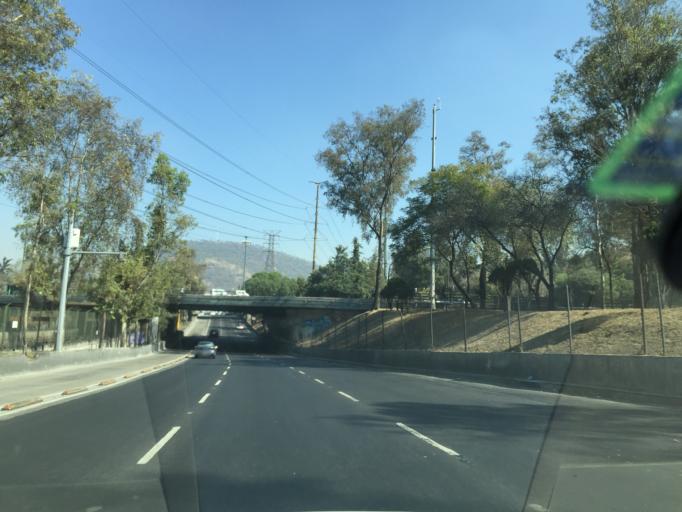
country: MX
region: Mexico
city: Colonia Lindavista
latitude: 19.4911
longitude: -99.1206
